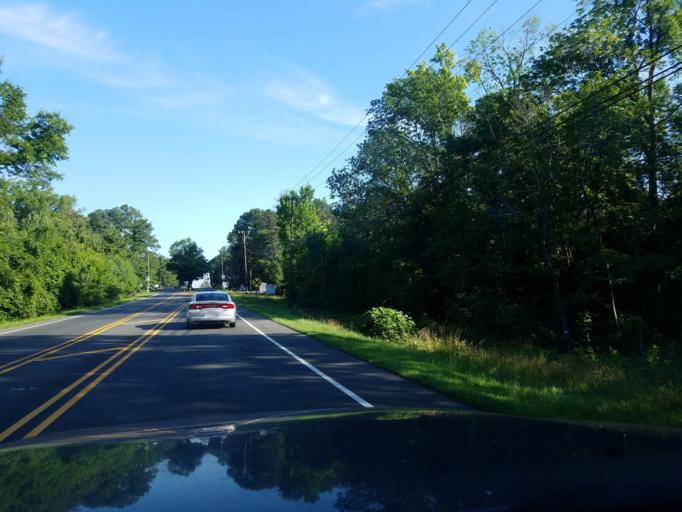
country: US
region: North Carolina
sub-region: Granville County
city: Butner
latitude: 36.1286
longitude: -78.7530
